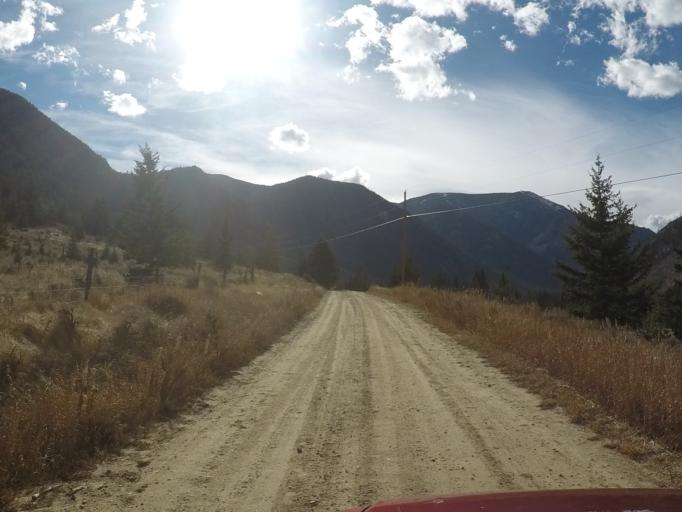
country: US
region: Montana
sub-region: Carbon County
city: Red Lodge
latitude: 45.0934
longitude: -109.3142
